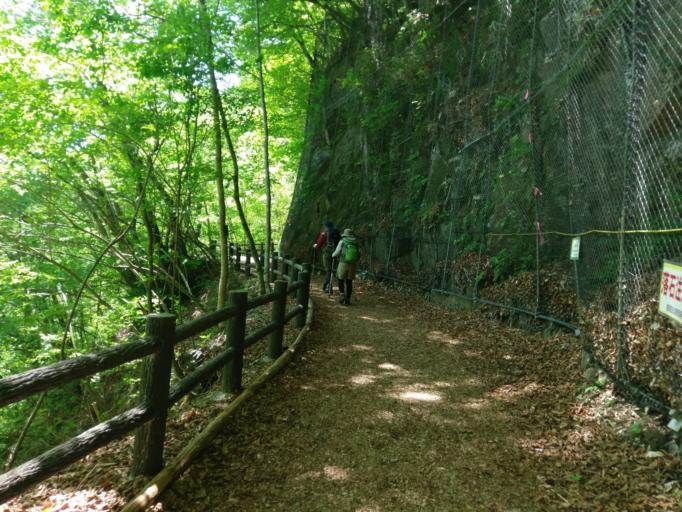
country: JP
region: Yamanashi
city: Uenohara
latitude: 35.7363
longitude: 139.0264
